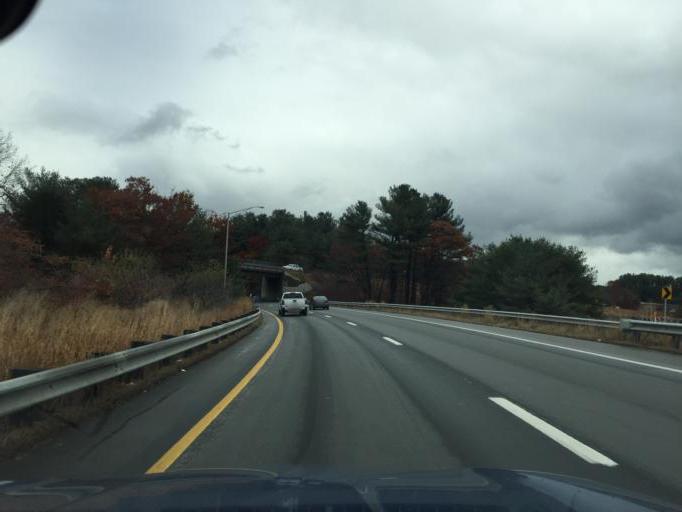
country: US
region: New Hampshire
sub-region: Hillsborough County
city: Manchester
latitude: 42.9611
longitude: -71.4169
